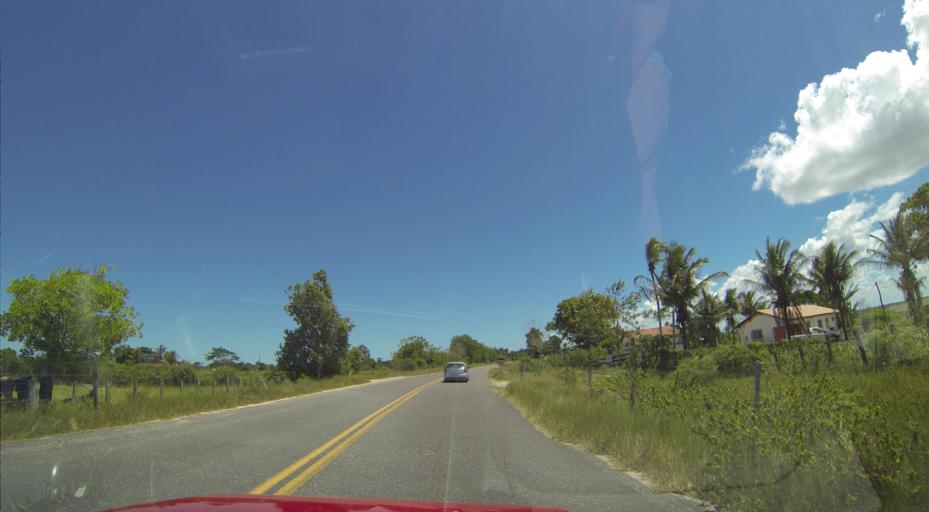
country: BR
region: Bahia
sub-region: Prado
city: Prado
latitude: -17.2121
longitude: -39.3876
